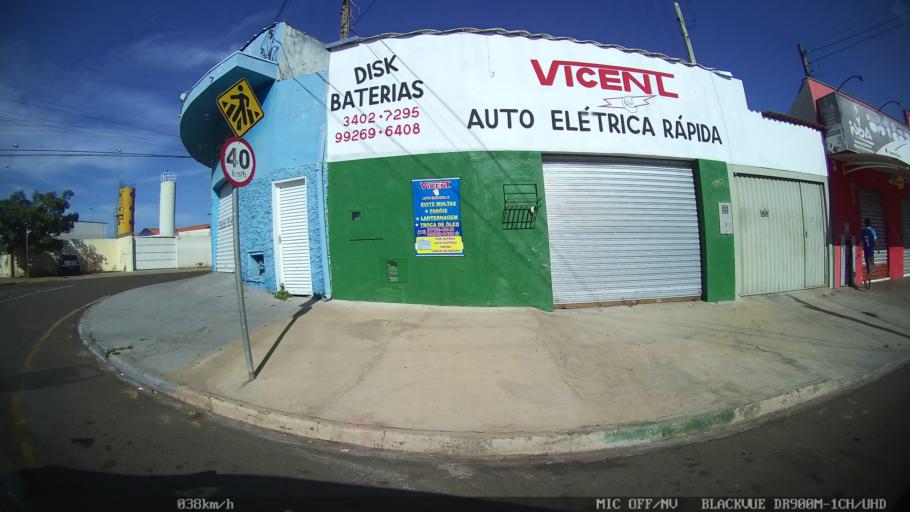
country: BR
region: Sao Paulo
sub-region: Franca
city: Franca
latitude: -20.4877
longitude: -47.4208
